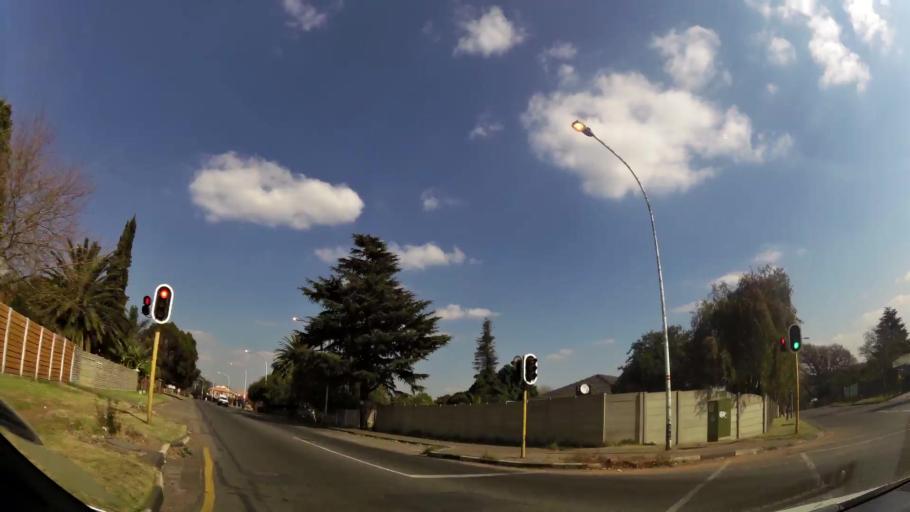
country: ZA
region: Gauteng
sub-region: Ekurhuleni Metropolitan Municipality
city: Boksburg
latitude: -26.1819
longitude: 28.2080
